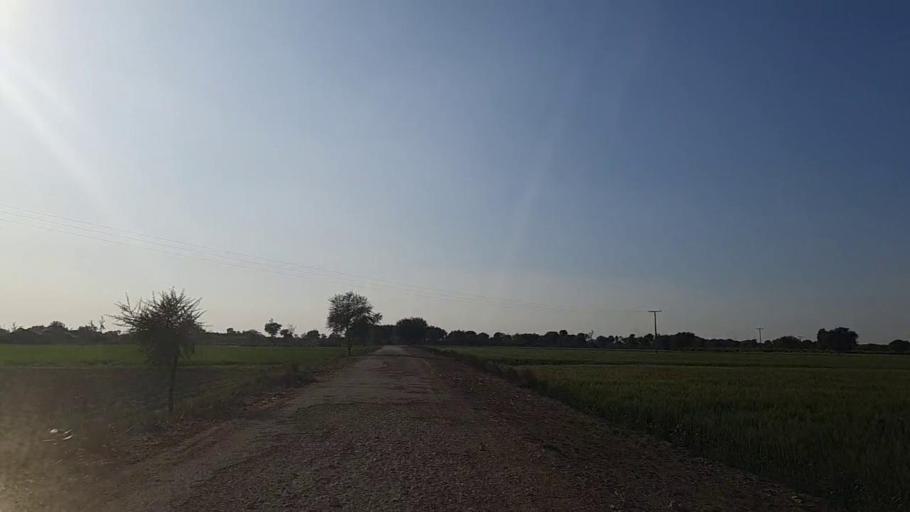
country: PK
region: Sindh
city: Shahpur Chakar
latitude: 26.1927
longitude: 68.6391
